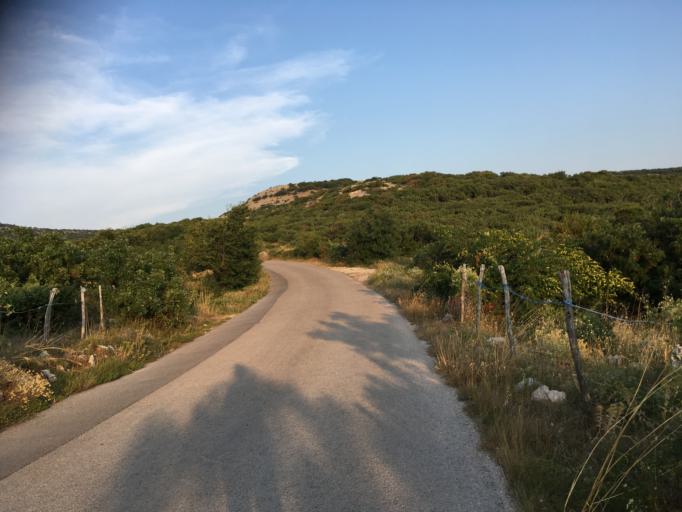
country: HR
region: Primorsko-Goranska
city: Punat
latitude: 44.9920
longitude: 14.6340
